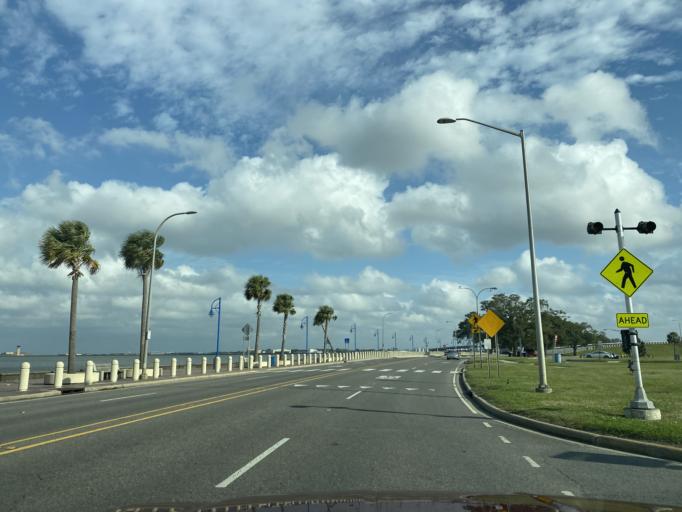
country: US
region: Louisiana
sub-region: Orleans Parish
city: New Orleans
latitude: 30.0353
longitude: -90.0438
